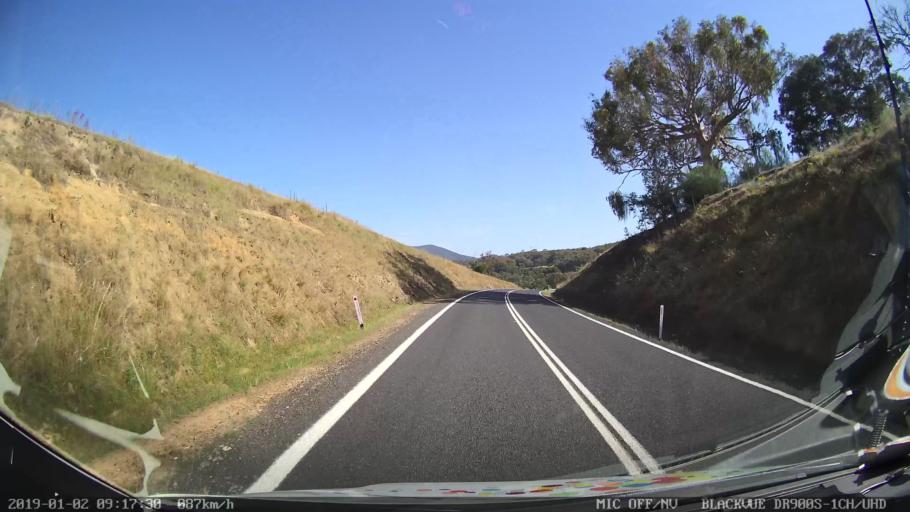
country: AU
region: New South Wales
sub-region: Tumut Shire
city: Tumut
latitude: -35.4397
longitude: 148.2866
